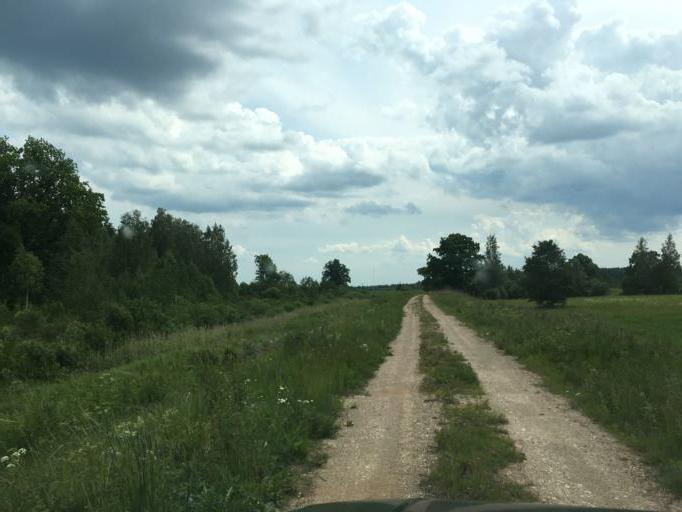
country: LV
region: Rugaju
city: Rugaji
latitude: 56.9778
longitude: 27.0504
